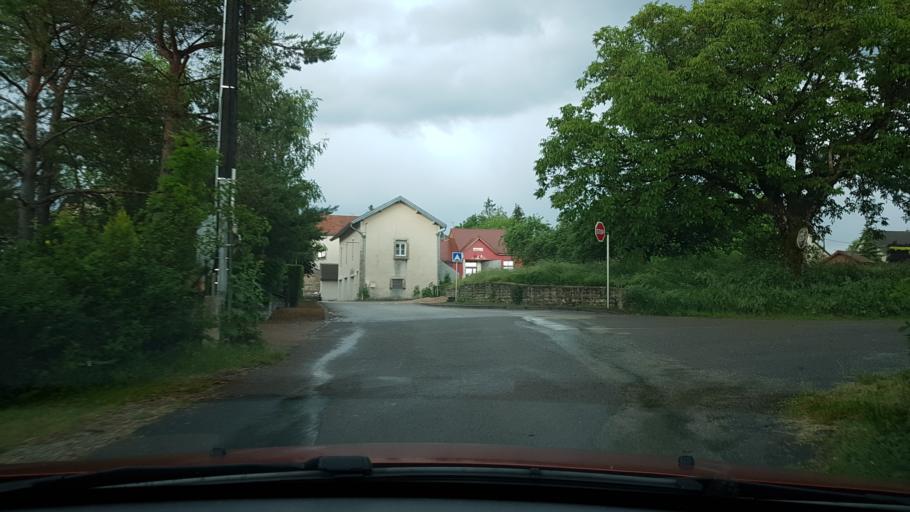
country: FR
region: Franche-Comte
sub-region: Departement du Jura
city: Clairvaux-les-Lacs
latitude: 46.5496
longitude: 5.7095
